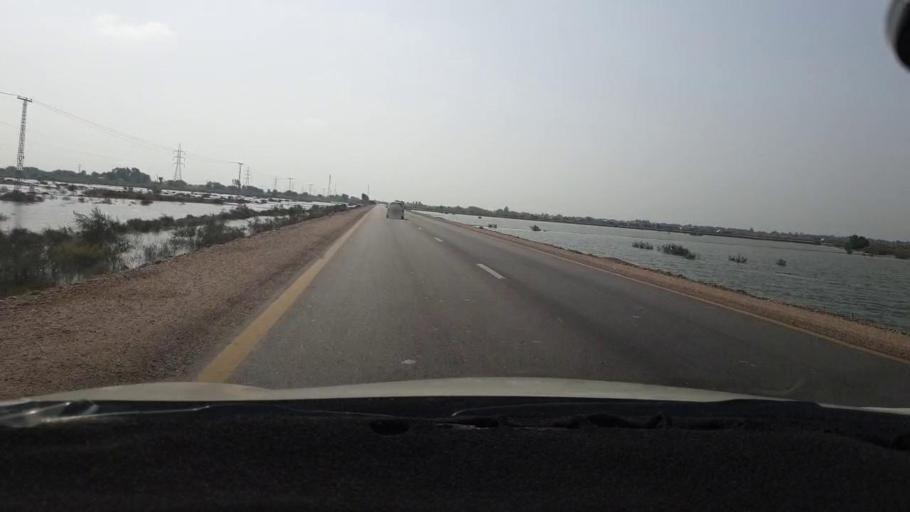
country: PK
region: Sindh
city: Jhol
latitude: 25.8950
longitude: 69.0269
